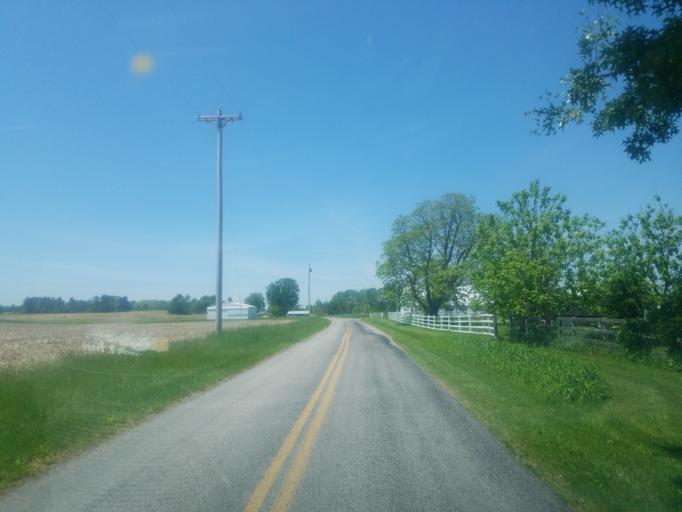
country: US
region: Ohio
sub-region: Huron County
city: New London
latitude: 41.1164
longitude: -82.4339
